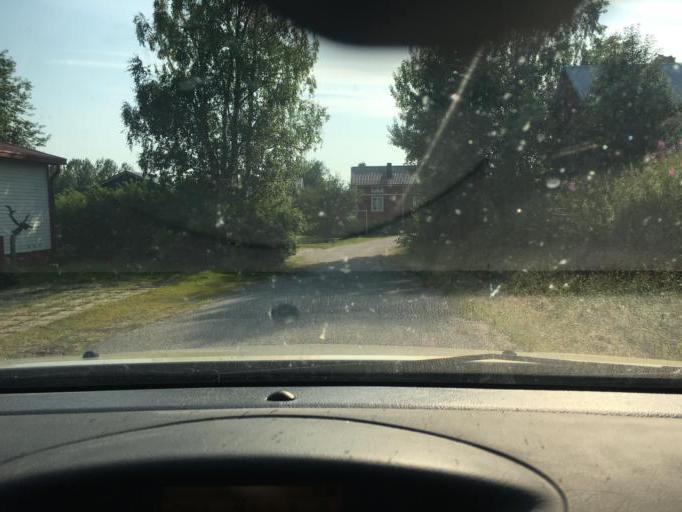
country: SE
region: Norrbotten
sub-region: Kalix Kommun
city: Toere
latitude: 66.0702
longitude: 22.7133
